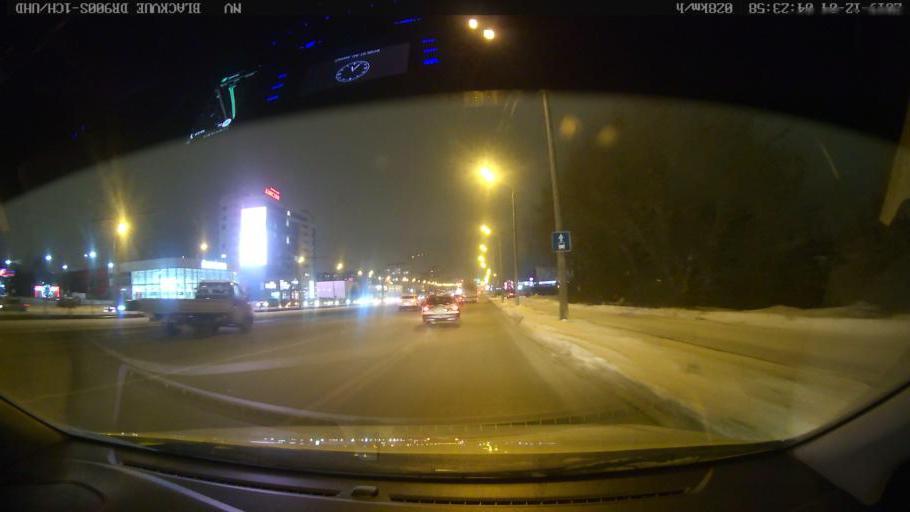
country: RU
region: Tatarstan
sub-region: Gorod Kazan'
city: Kazan
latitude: 55.7991
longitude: 49.2143
